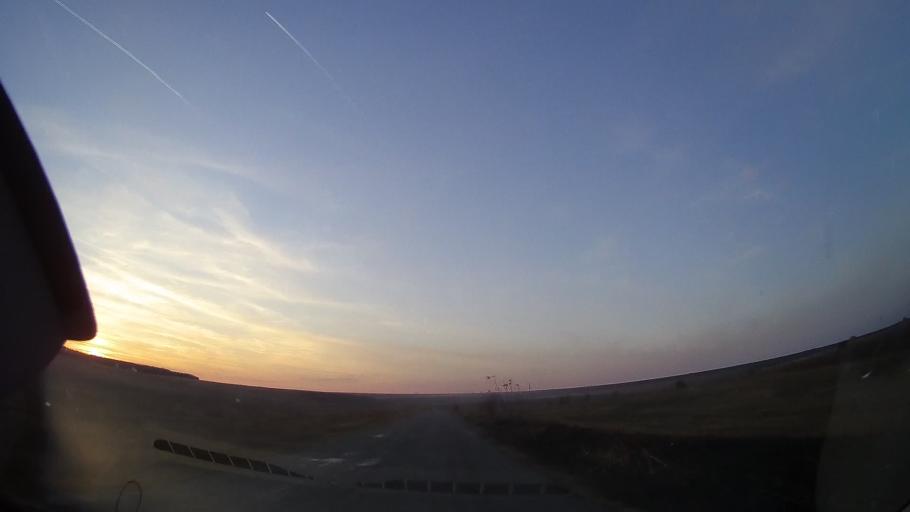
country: RO
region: Constanta
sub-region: Comuna Mereni
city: Mereni
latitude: 44.0174
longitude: 28.3032
